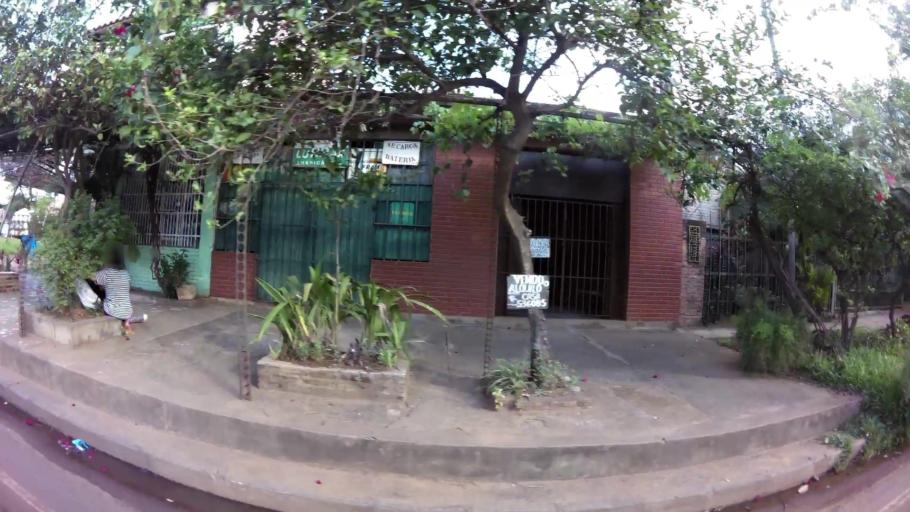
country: PY
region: Central
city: Fernando de la Mora
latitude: -25.3546
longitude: -57.5408
